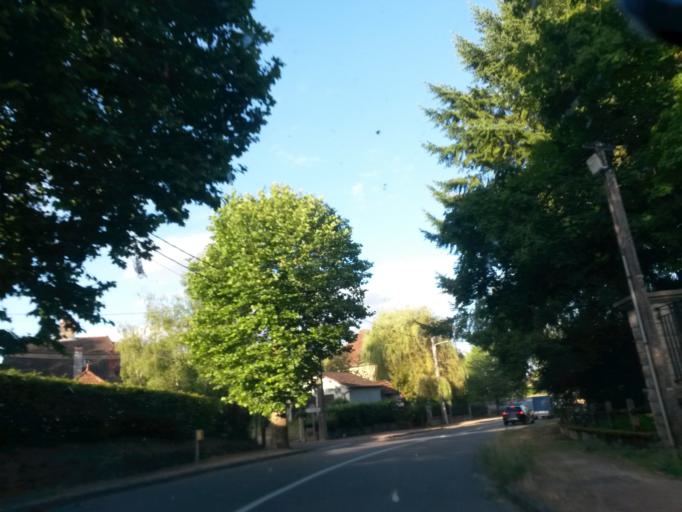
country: FR
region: Bourgogne
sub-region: Departement de la Nievre
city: Premery
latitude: 47.1737
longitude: 3.3247
